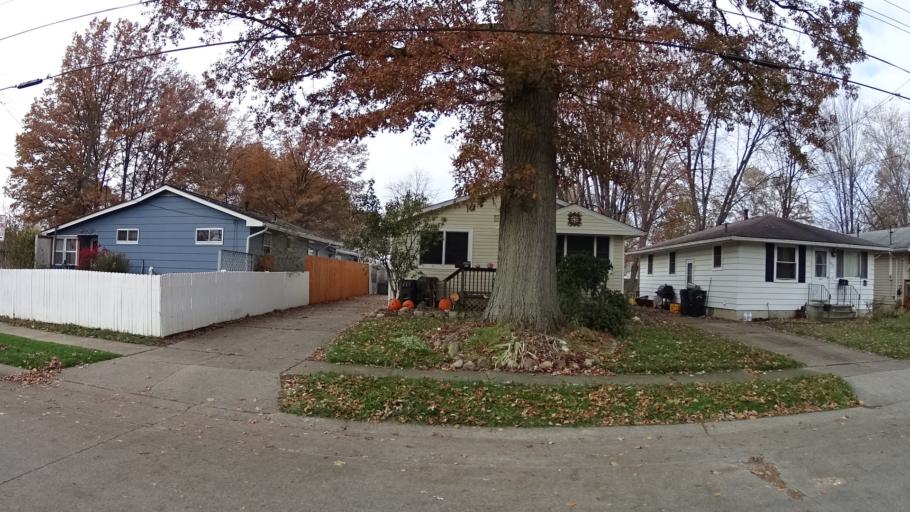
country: US
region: Ohio
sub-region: Lorain County
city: Elyria
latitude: 41.3598
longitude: -82.0792
